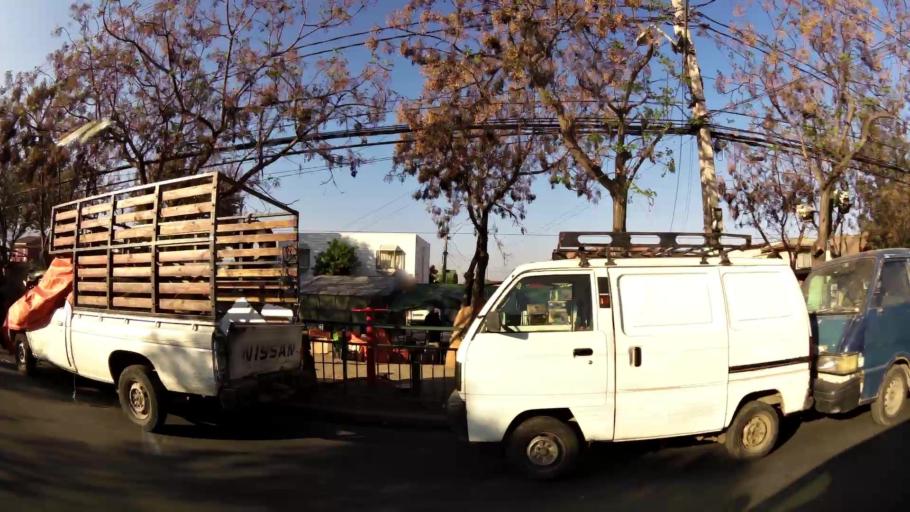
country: CL
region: Santiago Metropolitan
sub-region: Provincia de Santiago
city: Santiago
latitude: -33.3752
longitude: -70.6327
